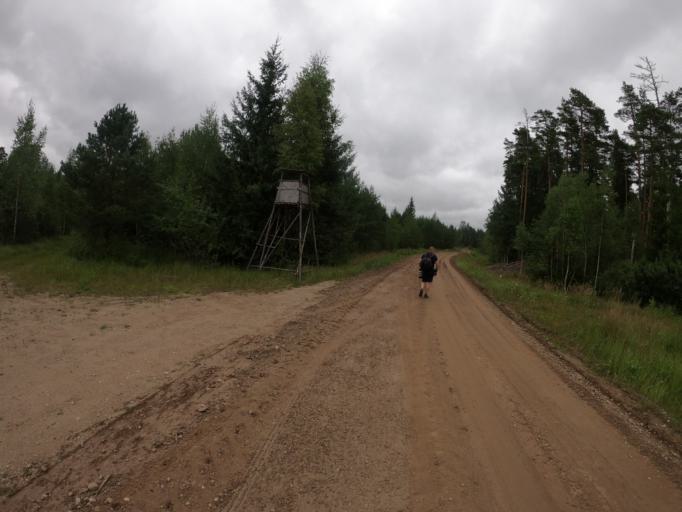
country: LV
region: Kuldigas Rajons
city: Kuldiga
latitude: 57.0435
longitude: 22.0700
